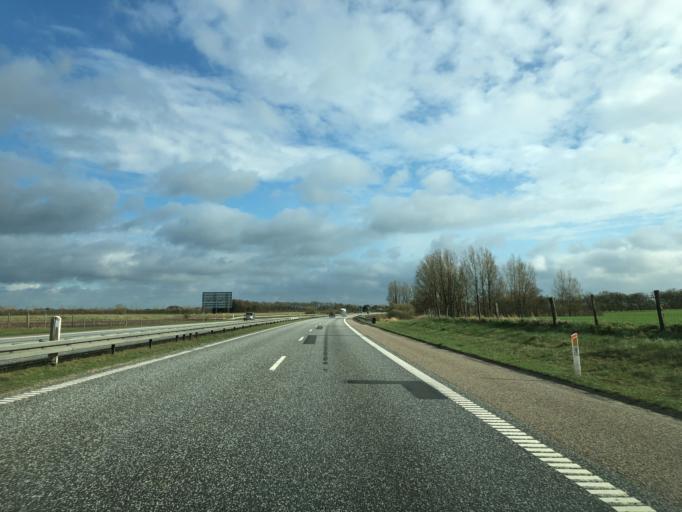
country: DK
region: North Denmark
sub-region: Alborg Kommune
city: Vestbjerg
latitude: 57.1911
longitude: 9.9387
